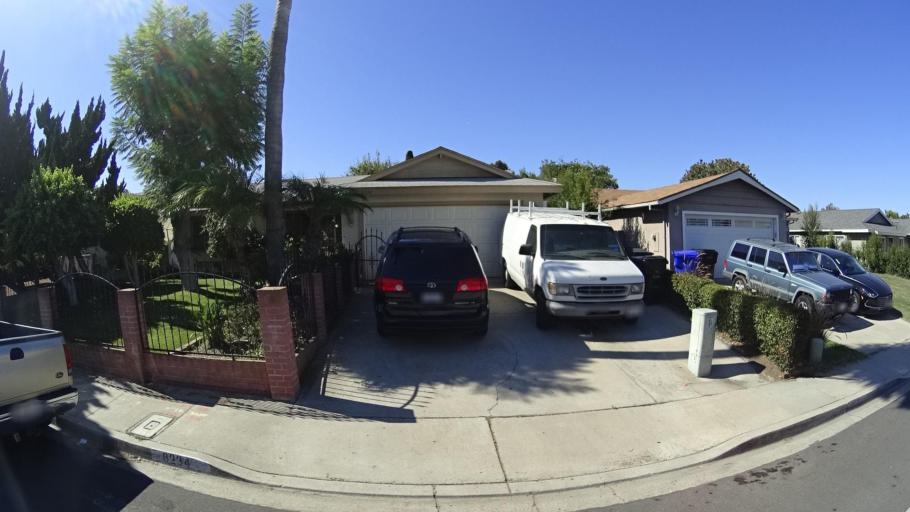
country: US
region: California
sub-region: San Diego County
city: La Presa
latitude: 32.7027
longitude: -117.0253
